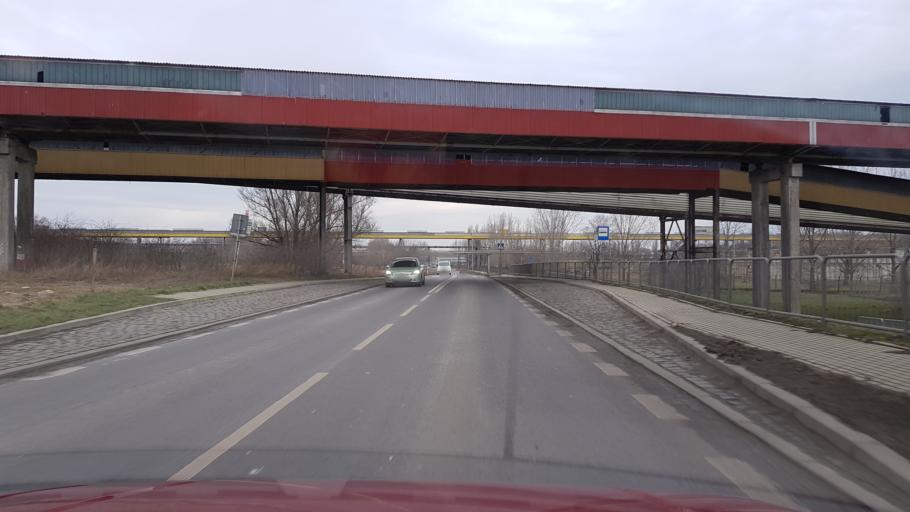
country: PL
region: West Pomeranian Voivodeship
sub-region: Powiat policki
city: Police
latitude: 53.5736
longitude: 14.5559
